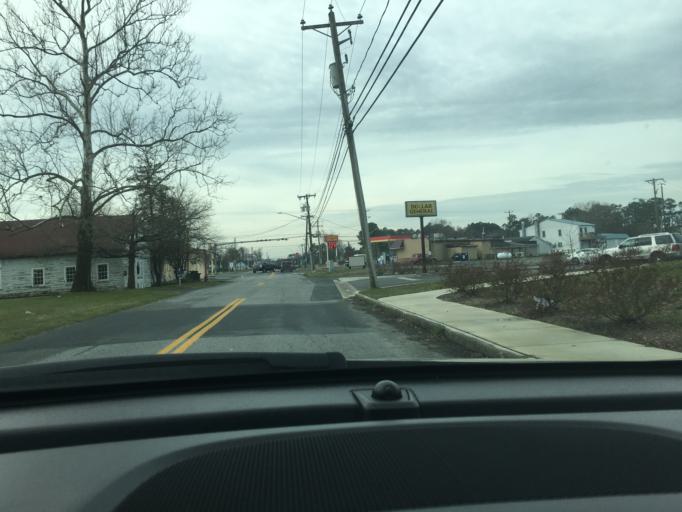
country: US
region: Maryland
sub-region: Wicomico County
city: Pittsville
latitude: 38.3898
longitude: -75.3517
